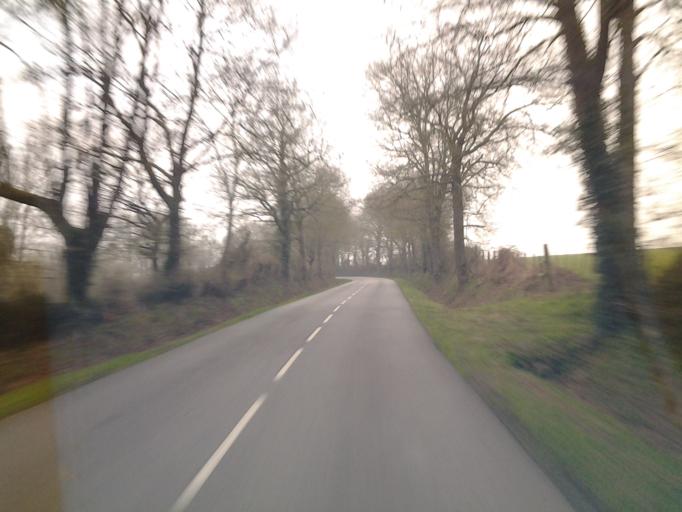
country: FR
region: Pays de la Loire
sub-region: Departement de la Vendee
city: Nesmy
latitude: 46.6207
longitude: -1.4086
